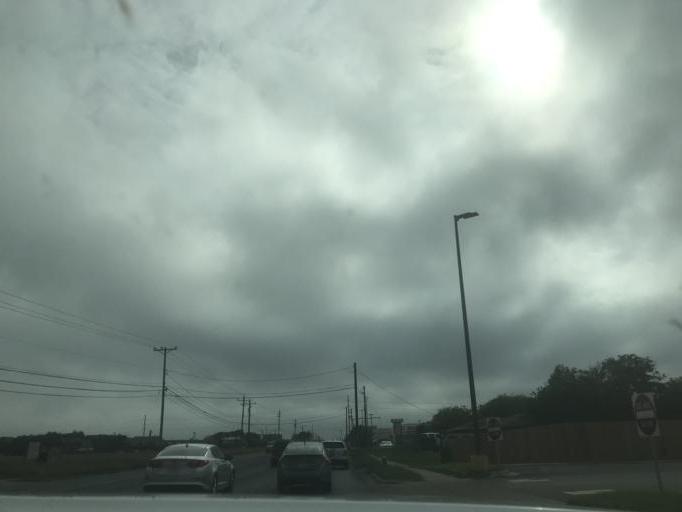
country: US
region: Texas
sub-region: Nueces County
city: Corpus Christi
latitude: 27.6916
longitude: -97.3635
